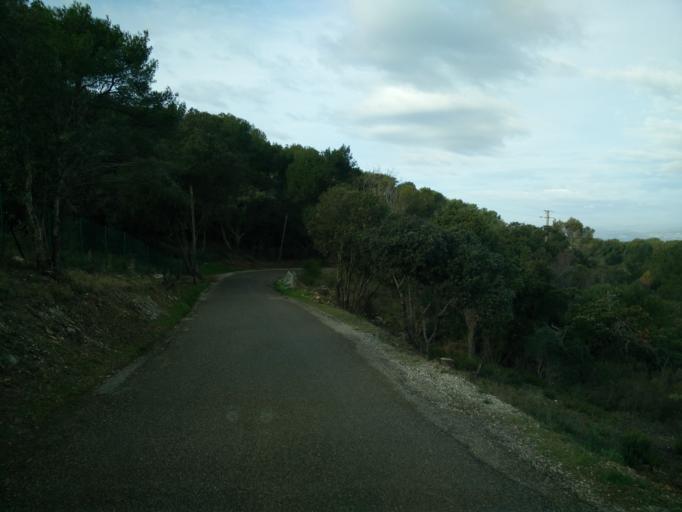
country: FR
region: Provence-Alpes-Cote d'Azur
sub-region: Departement du Var
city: Six-Fours-les-Plages
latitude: 43.0670
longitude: 5.8279
